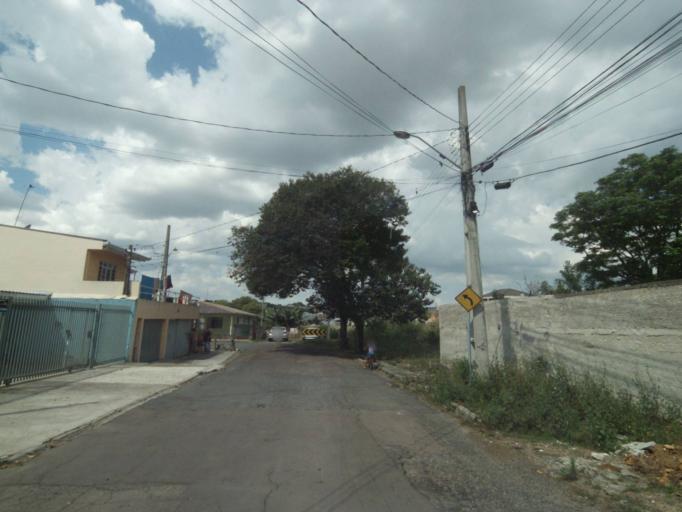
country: BR
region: Parana
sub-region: Sao Jose Dos Pinhais
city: Sao Jose dos Pinhais
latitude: -25.5343
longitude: -49.2567
